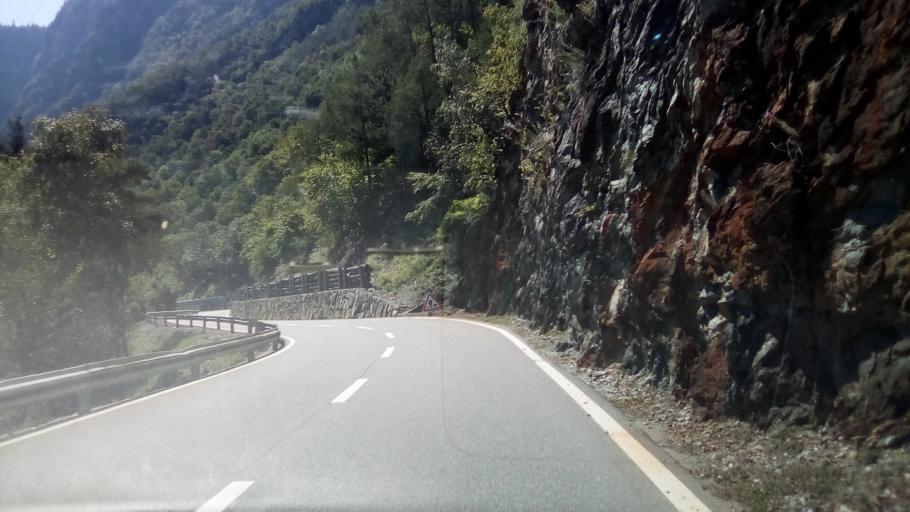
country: CH
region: Valais
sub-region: Saint-Maurice District
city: Vernayaz
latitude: 46.1211
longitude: 7.0431
